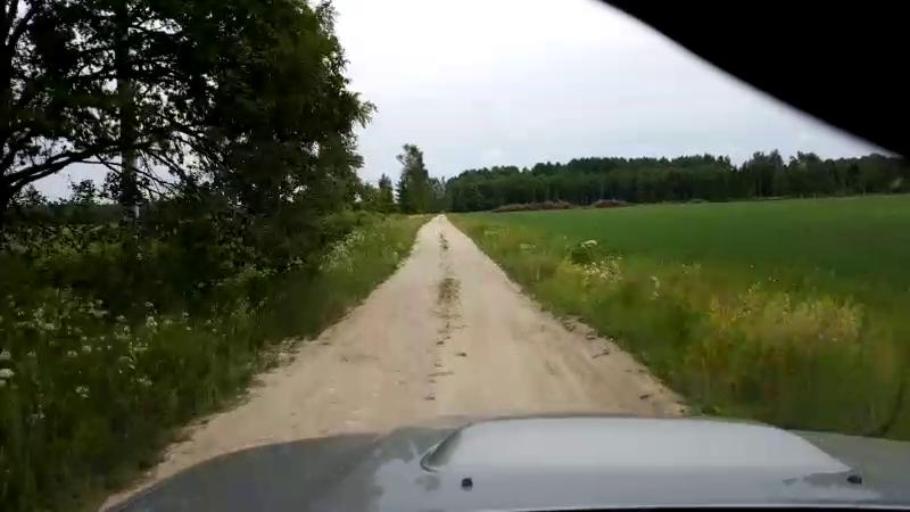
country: EE
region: Paernumaa
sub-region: Halinga vald
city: Parnu-Jaagupi
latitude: 58.5588
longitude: 24.6237
